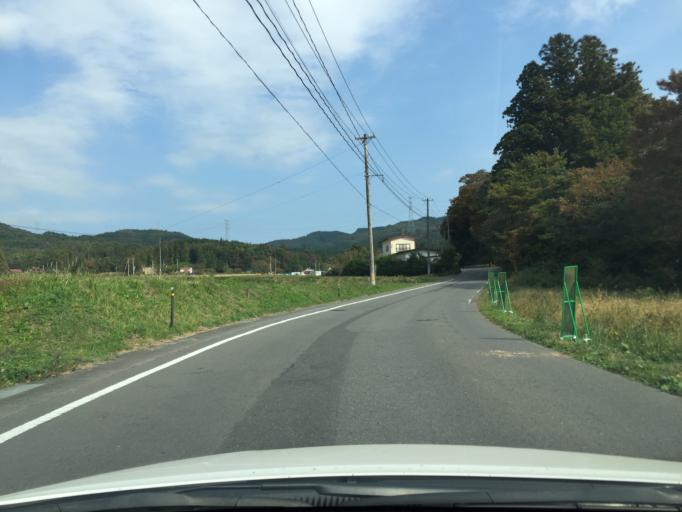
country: JP
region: Fukushima
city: Ishikawa
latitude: 36.9676
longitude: 140.4362
